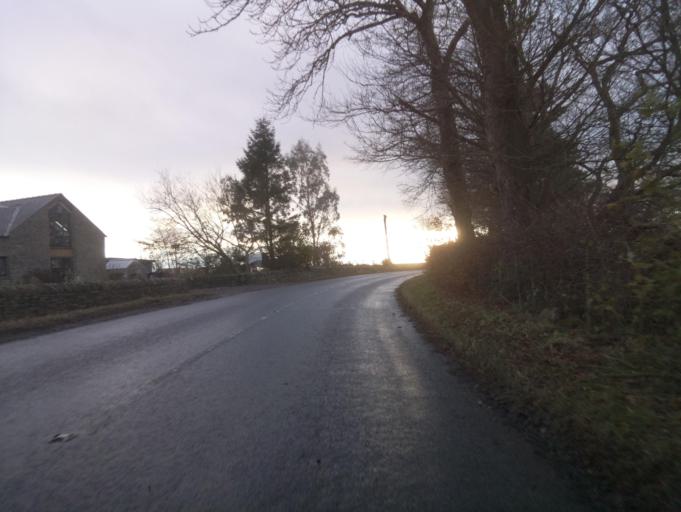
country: GB
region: Scotland
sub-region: Angus
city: Letham
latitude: 56.5306
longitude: -2.7973
